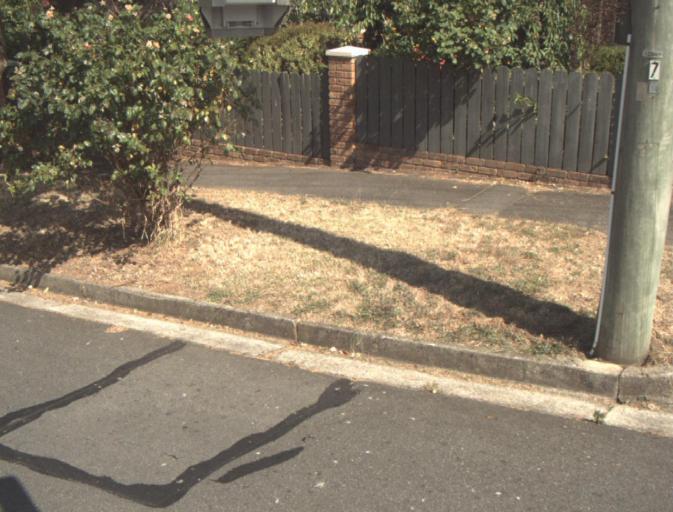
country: AU
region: Tasmania
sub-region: Launceston
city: East Launceston
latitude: -41.4729
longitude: 147.1648
